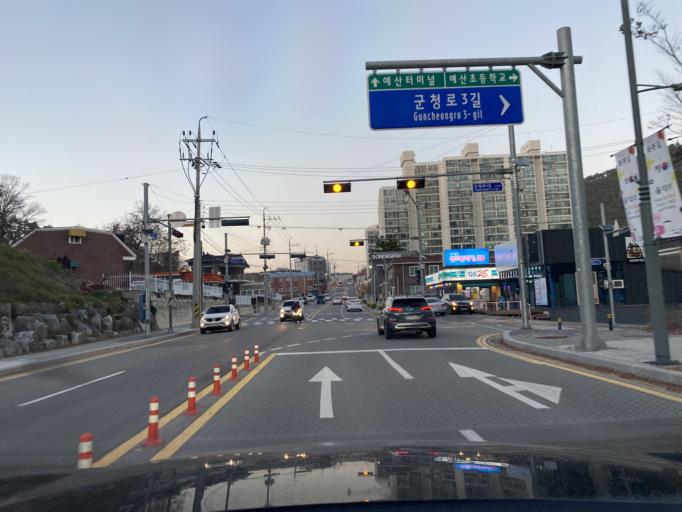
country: KR
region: Chungcheongnam-do
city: Yesan
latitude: 36.6825
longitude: 126.8436
